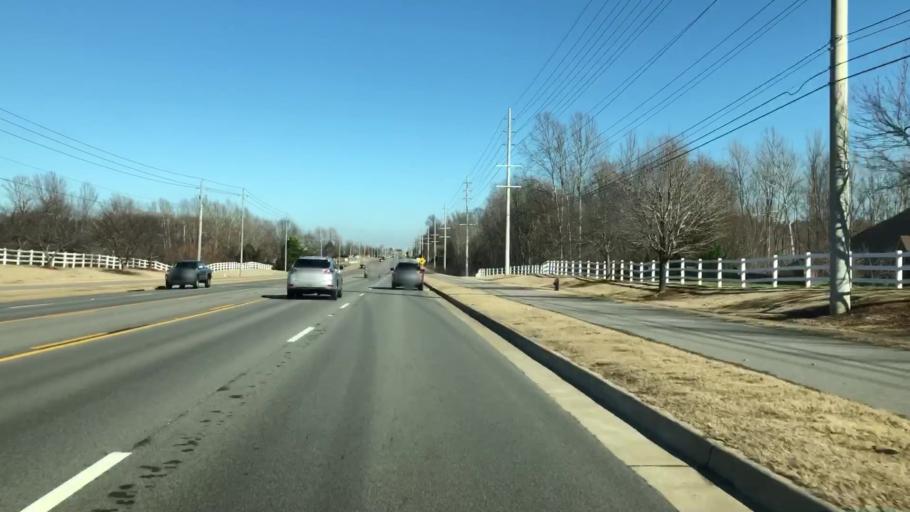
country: US
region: Alabama
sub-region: Madison County
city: Madison
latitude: 34.7129
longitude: -86.7864
